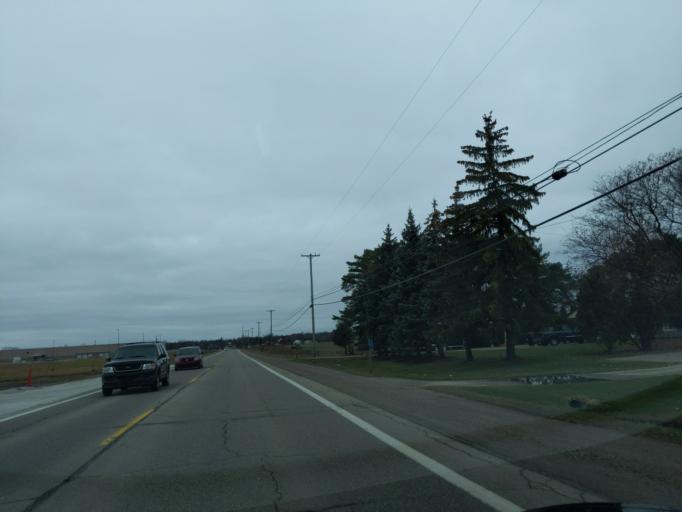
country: US
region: Michigan
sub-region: Clinton County
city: Saint Johns
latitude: 43.0014
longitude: -84.5297
